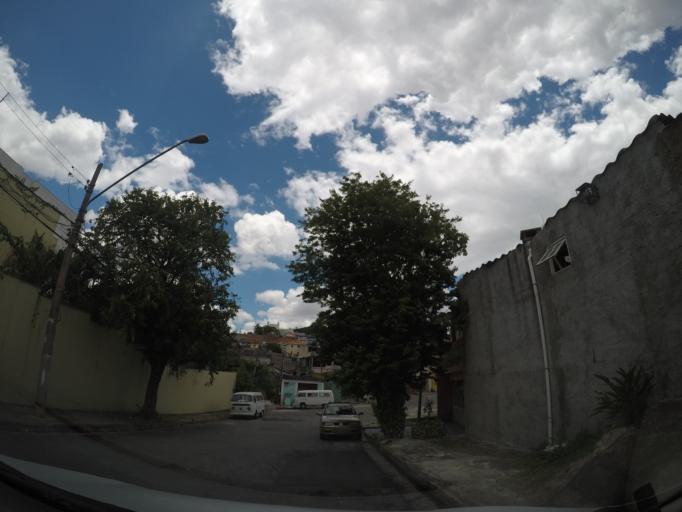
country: BR
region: Sao Paulo
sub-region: Guarulhos
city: Guarulhos
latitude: -23.4703
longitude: -46.5403
